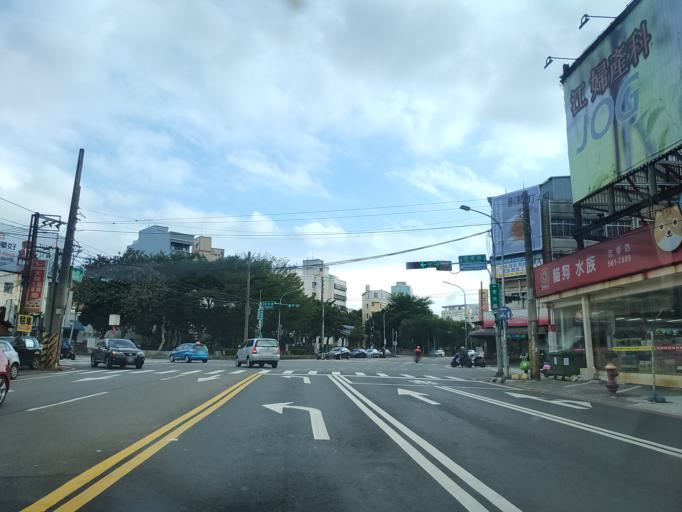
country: TW
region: Taiwan
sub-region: Hsinchu
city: Hsinchu
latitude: 24.8059
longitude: 120.9864
